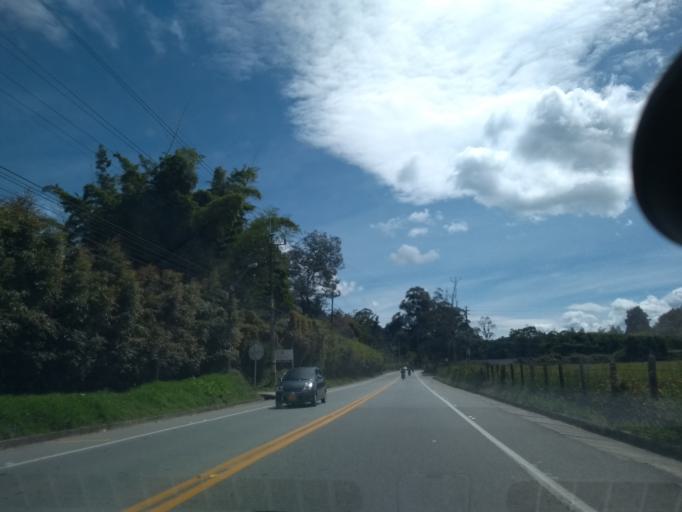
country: CO
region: Antioquia
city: Rionegro
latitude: 6.1037
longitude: -75.3848
